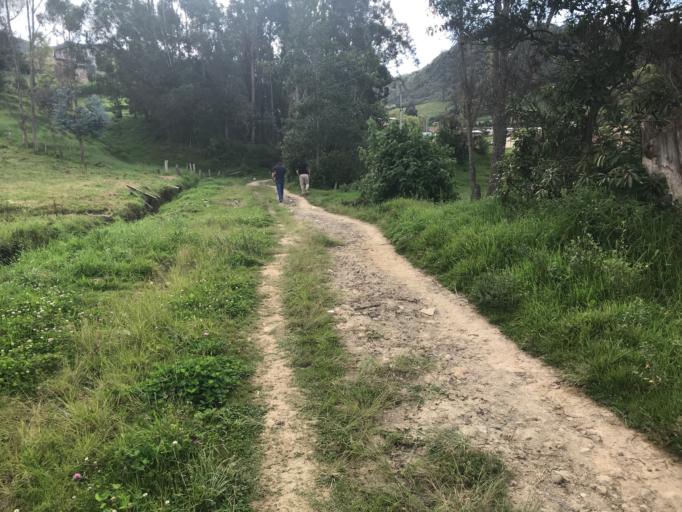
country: PE
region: Cajamarca
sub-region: Provincia de Chota
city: Querocoto
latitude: -6.3586
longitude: -79.0326
